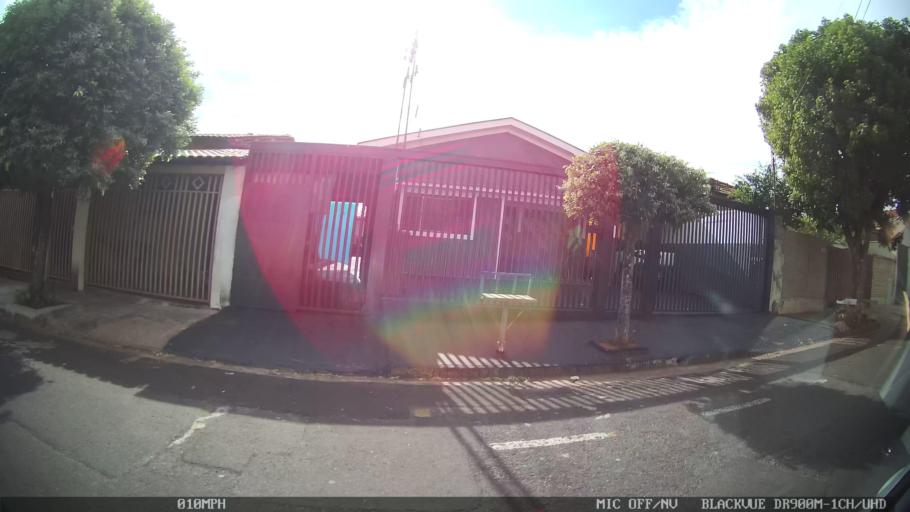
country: BR
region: Sao Paulo
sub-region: Sao Jose Do Rio Preto
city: Sao Jose do Rio Preto
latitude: -20.8313
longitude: -49.3792
